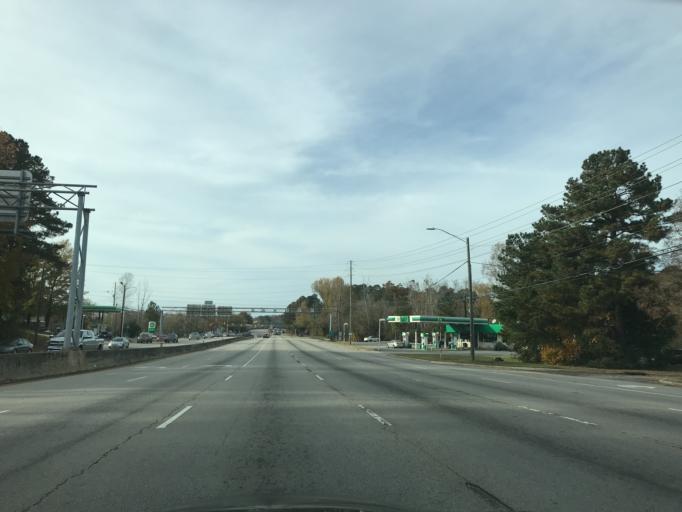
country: US
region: North Carolina
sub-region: Wake County
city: West Raleigh
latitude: 35.8368
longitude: -78.6716
